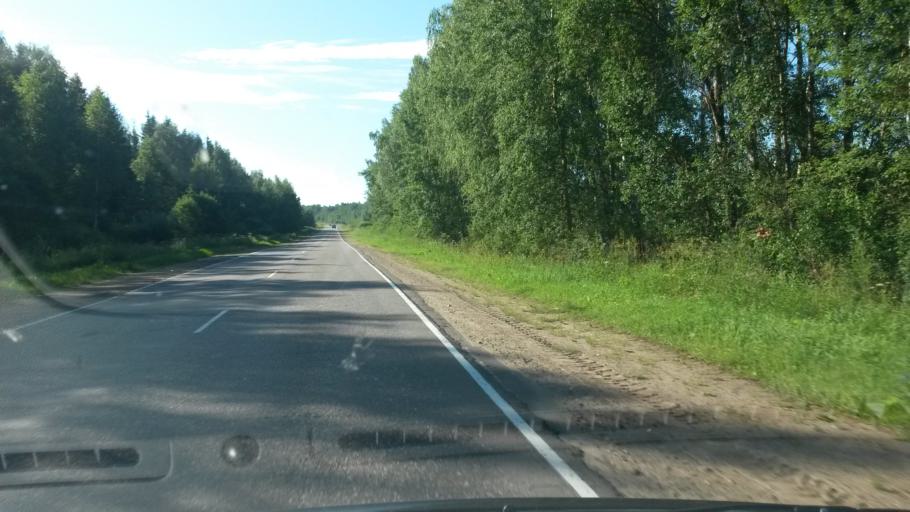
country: RU
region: Ivanovo
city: Pistsovo
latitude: 57.1459
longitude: 40.5719
